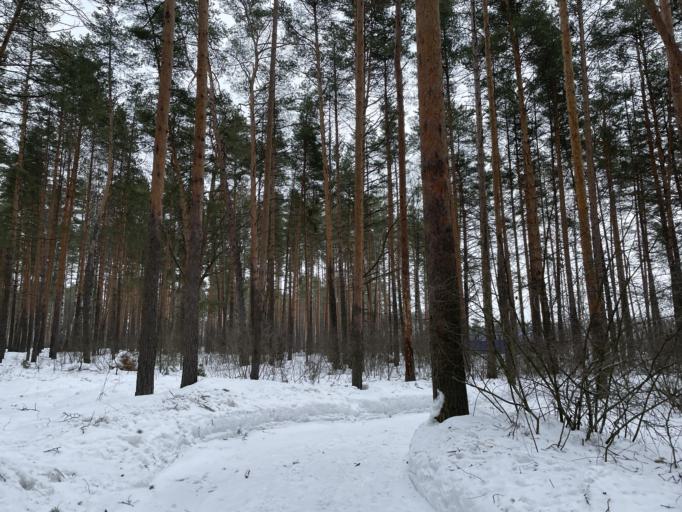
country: RU
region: Vladimir
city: Pokrov
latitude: 55.9377
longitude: 39.2376
